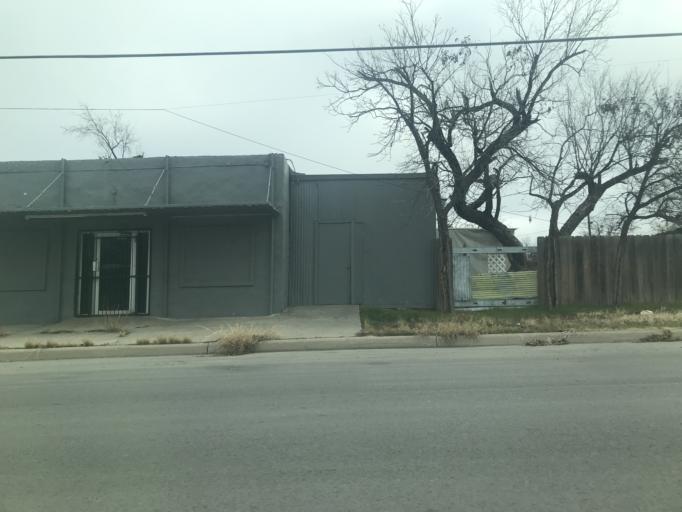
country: US
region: Texas
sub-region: Tom Green County
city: San Angelo
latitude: 31.4720
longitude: -100.4480
